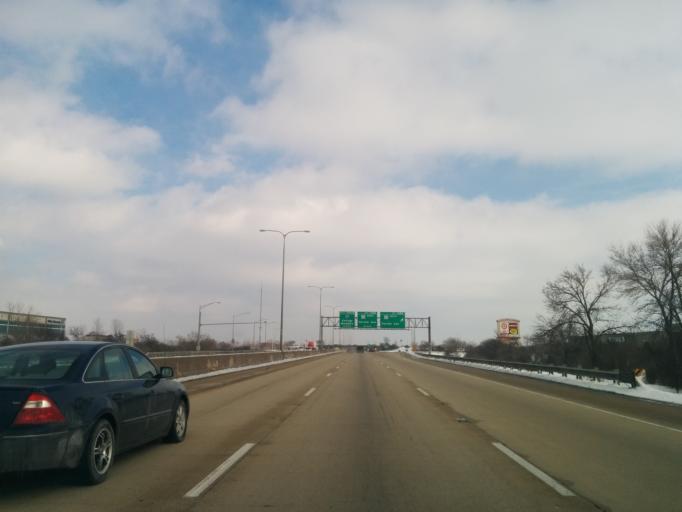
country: US
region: Illinois
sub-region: Cook County
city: Tinley Park
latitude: 41.5509
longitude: -87.8010
